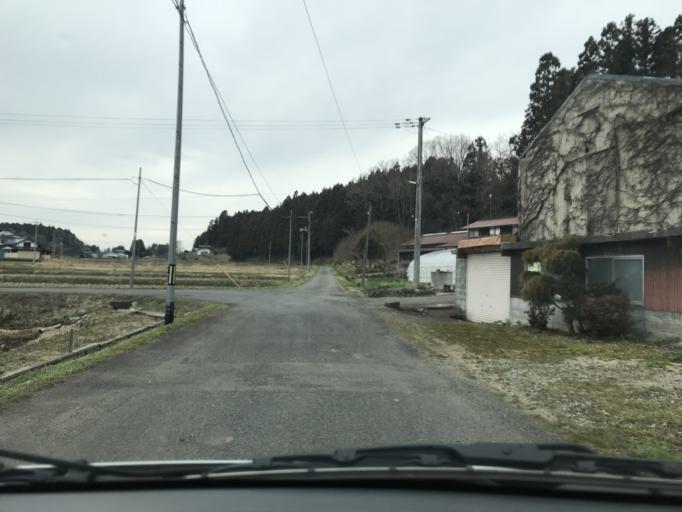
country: JP
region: Iwate
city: Mizusawa
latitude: 39.0948
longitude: 141.1107
